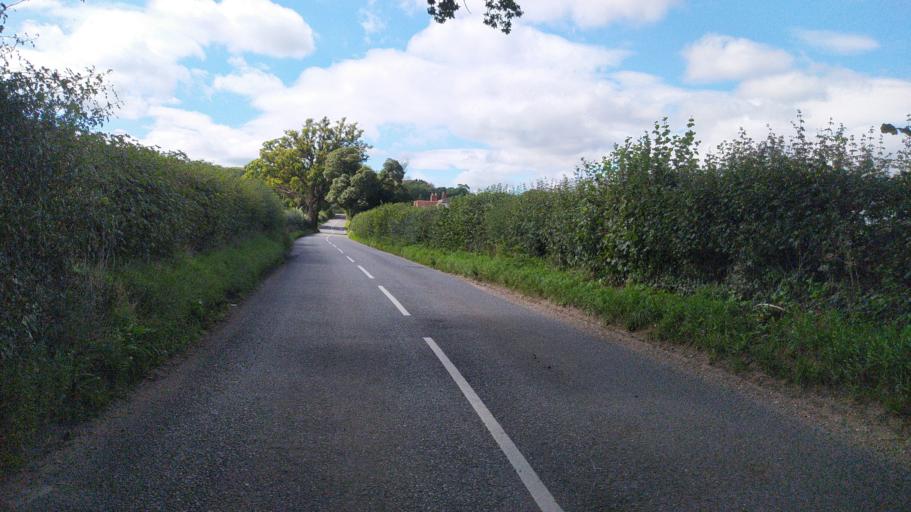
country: GB
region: England
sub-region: Hampshire
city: Romsey
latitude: 51.0070
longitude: -1.5048
